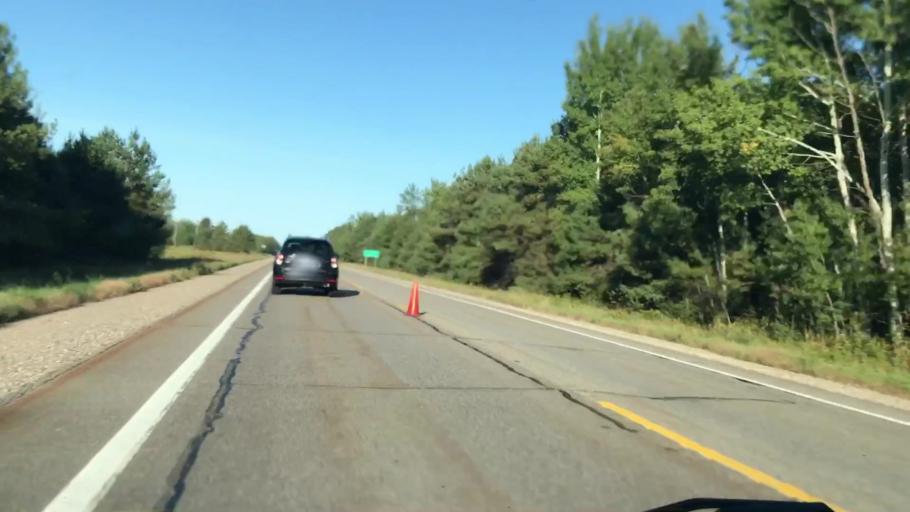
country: US
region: Michigan
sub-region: Chippewa County
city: Sault Ste. Marie
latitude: 46.3755
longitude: -84.6090
